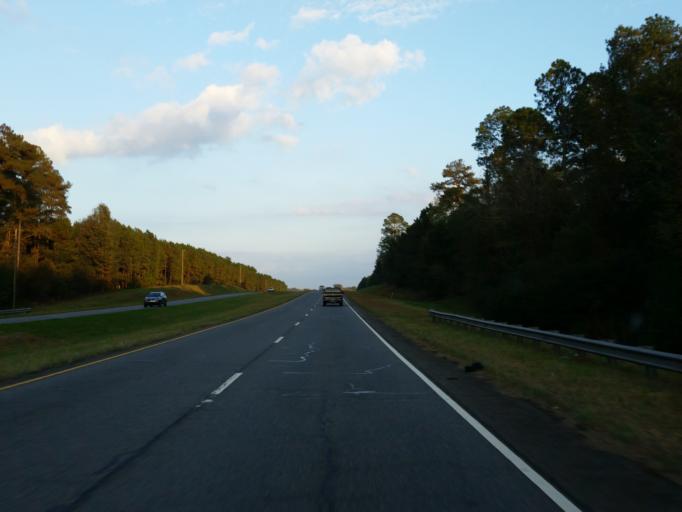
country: US
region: Georgia
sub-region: Houston County
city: Perry
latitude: 32.4129
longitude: -83.6626
